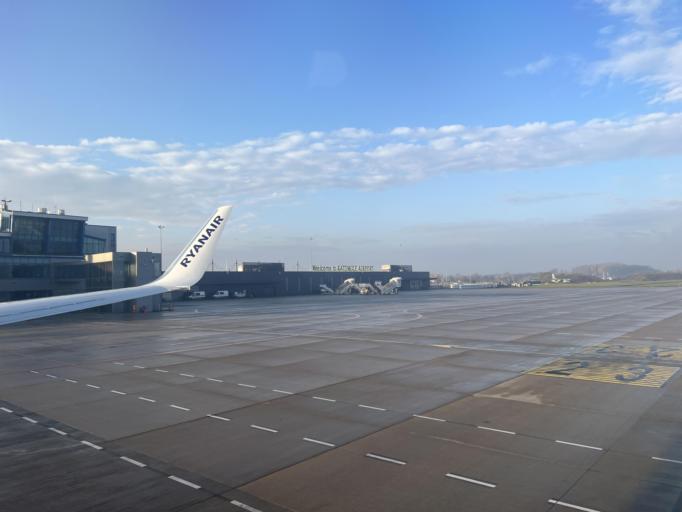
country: PL
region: Silesian Voivodeship
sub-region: Powiat tarnogorski
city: Ozarowice
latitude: 50.4724
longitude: 19.0719
